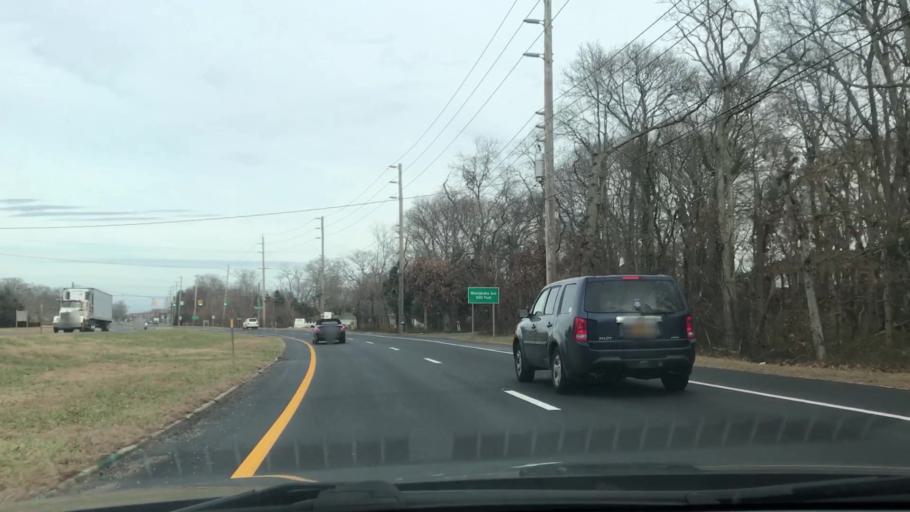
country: US
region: New York
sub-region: Suffolk County
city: Mattituck
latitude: 40.9906
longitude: -72.5401
